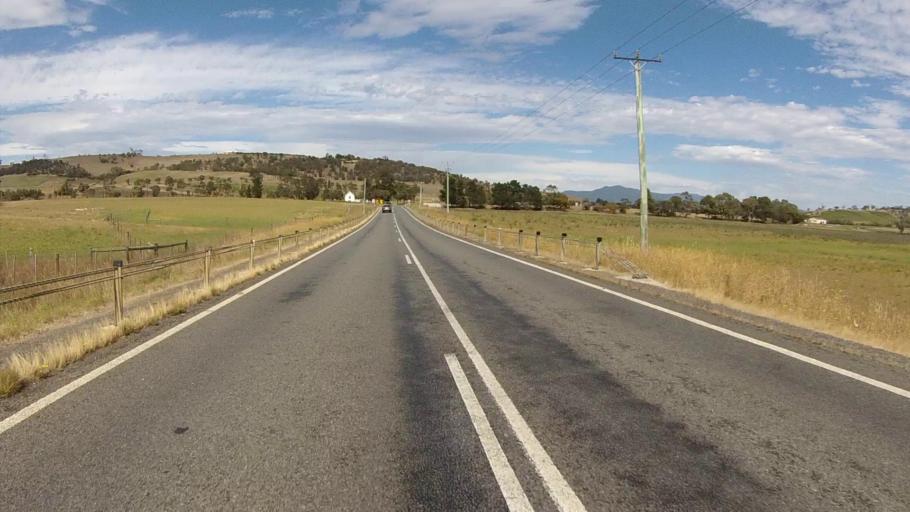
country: AU
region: Tasmania
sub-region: Brighton
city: Old Beach
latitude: -42.6896
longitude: 147.3483
